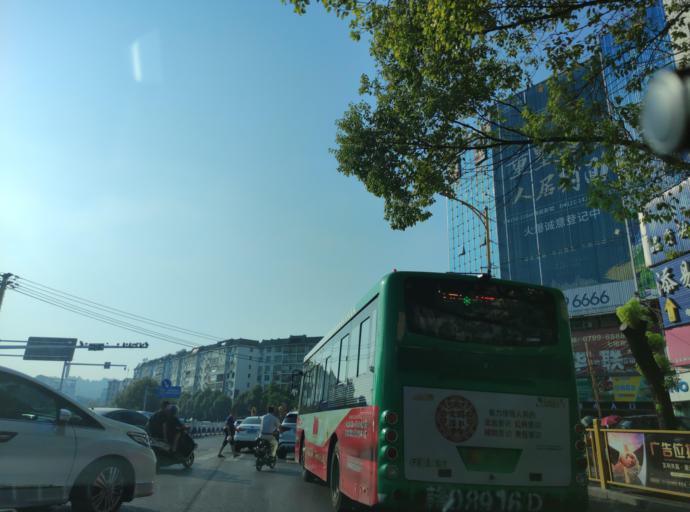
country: CN
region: Jiangxi Sheng
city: Pingxiang
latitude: 27.6299
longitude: 113.8503
